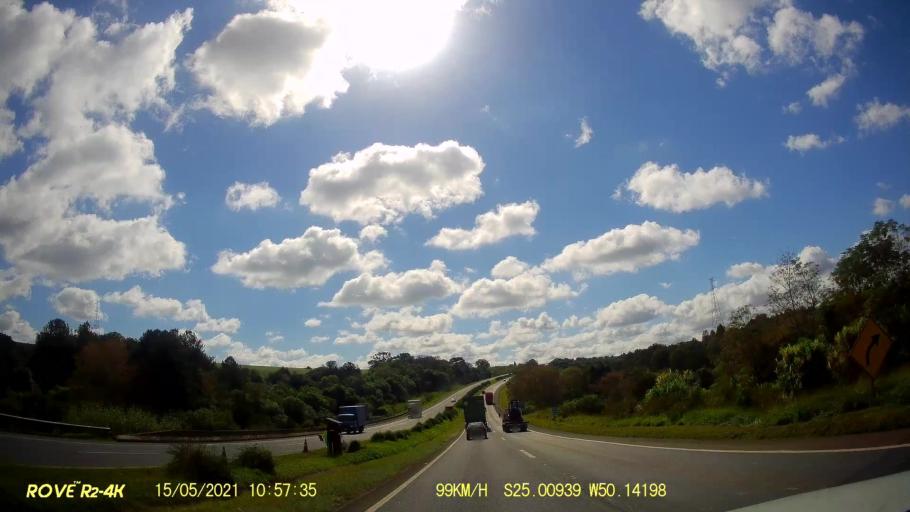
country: BR
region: Parana
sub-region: Carambei
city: Carambei
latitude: -25.0096
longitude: -50.1421
